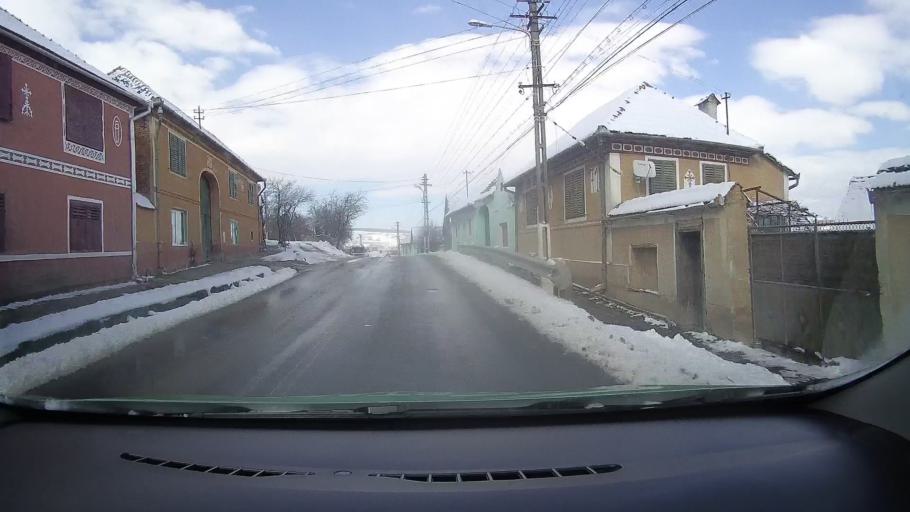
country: RO
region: Sibiu
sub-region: Comuna Altina
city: Altina
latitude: 45.9327
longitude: 24.4644
